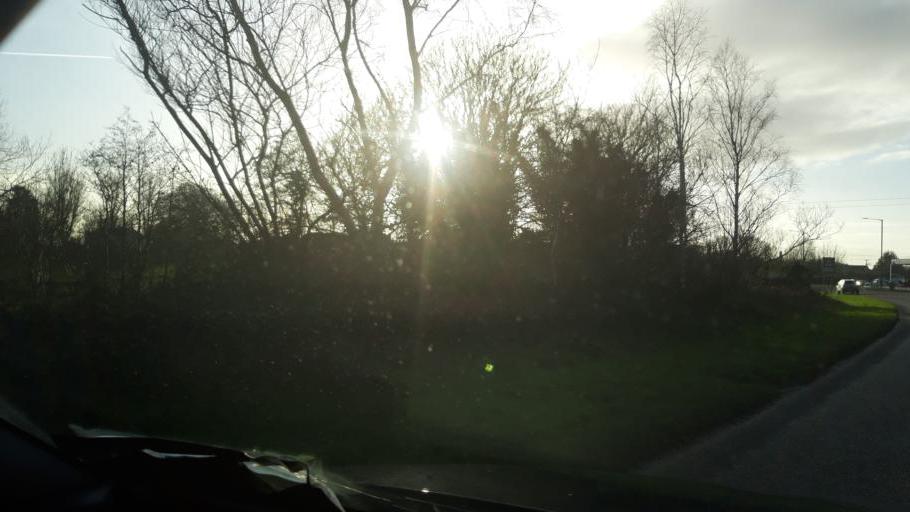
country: GB
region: Northern Ireland
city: Maghera
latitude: 54.8141
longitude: -6.7043
